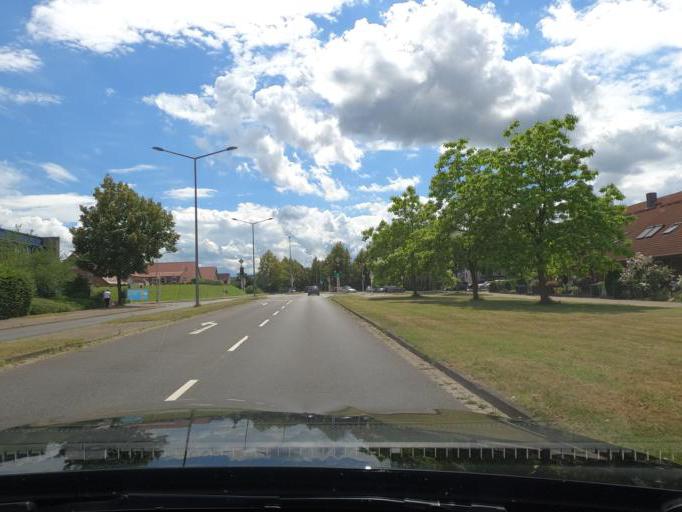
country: DE
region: Lower Saxony
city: Lengede
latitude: 52.1479
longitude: 10.2951
